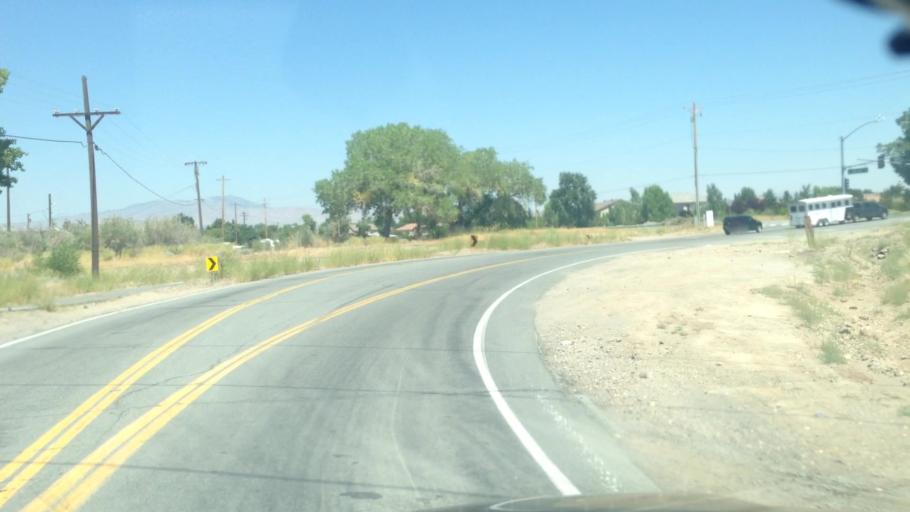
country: US
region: Nevada
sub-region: Storey County
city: Virginia City
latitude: 39.3966
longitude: -119.7358
